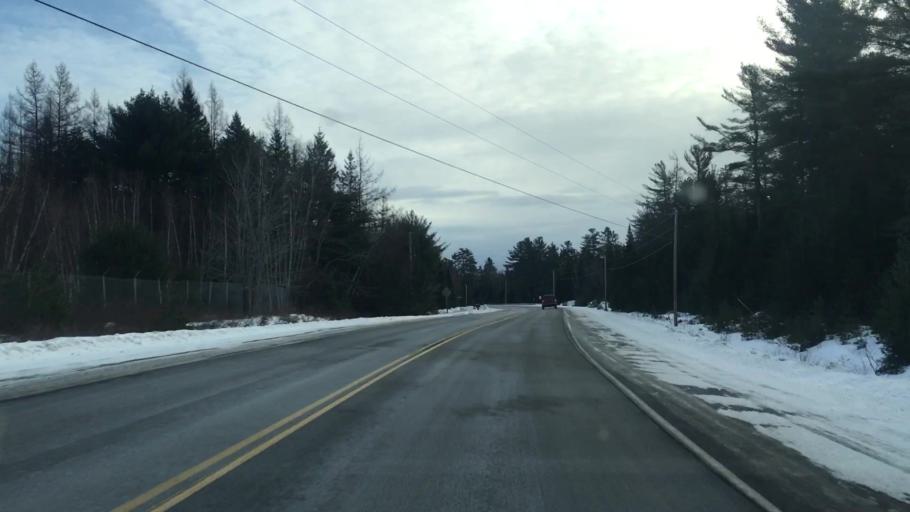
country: US
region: Maine
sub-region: Washington County
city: Addison
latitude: 44.9403
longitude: -67.7253
